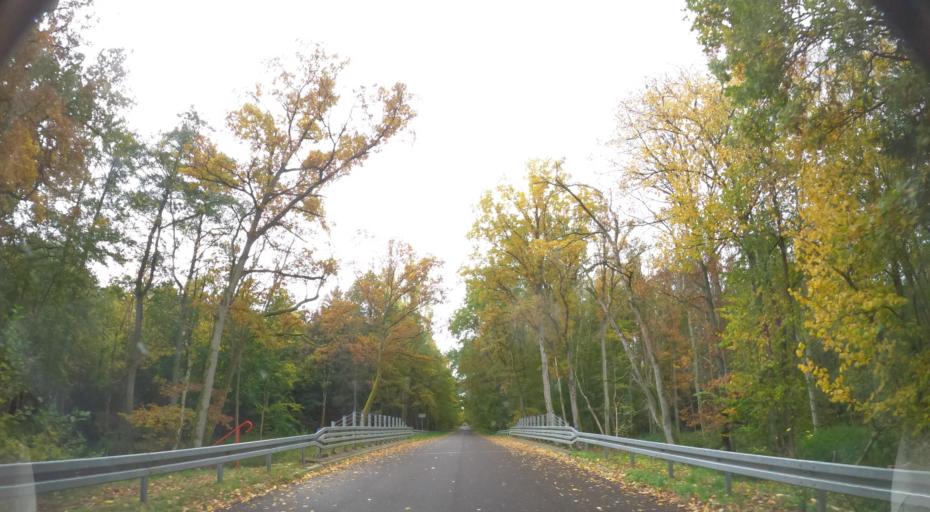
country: PL
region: West Pomeranian Voivodeship
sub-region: Powiat goleniowski
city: Stepnica
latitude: 53.6743
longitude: 14.6699
